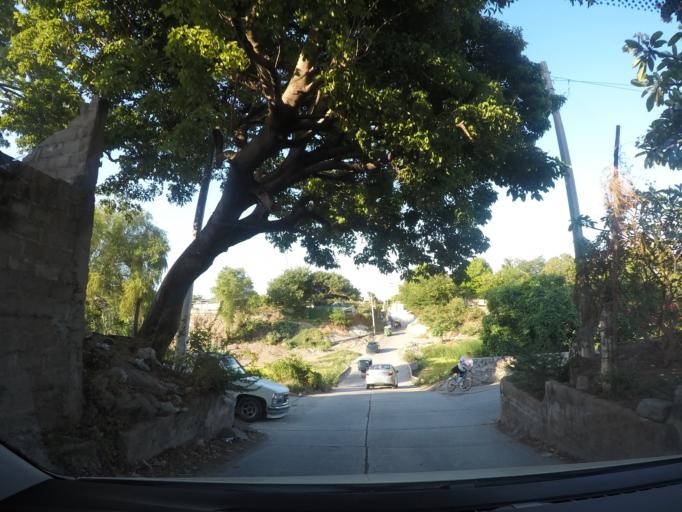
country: MX
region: Oaxaca
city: Juchitan de Zaragoza
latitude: 16.4398
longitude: -95.0258
